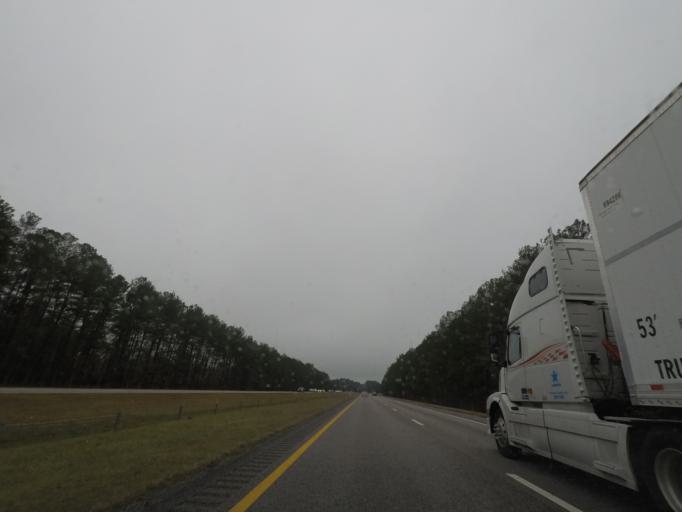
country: US
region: South Carolina
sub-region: Florence County
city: Timmonsville
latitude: 33.9989
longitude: -80.0087
